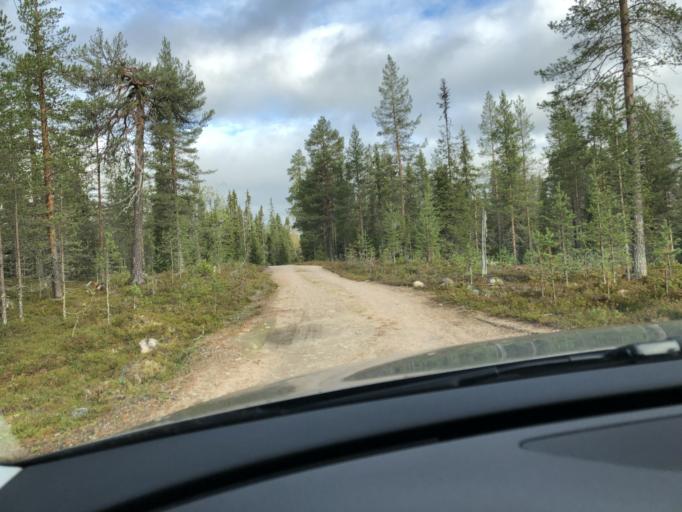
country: FI
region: Lapland
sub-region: Itae-Lappi
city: Posio
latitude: 66.0610
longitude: 27.8119
